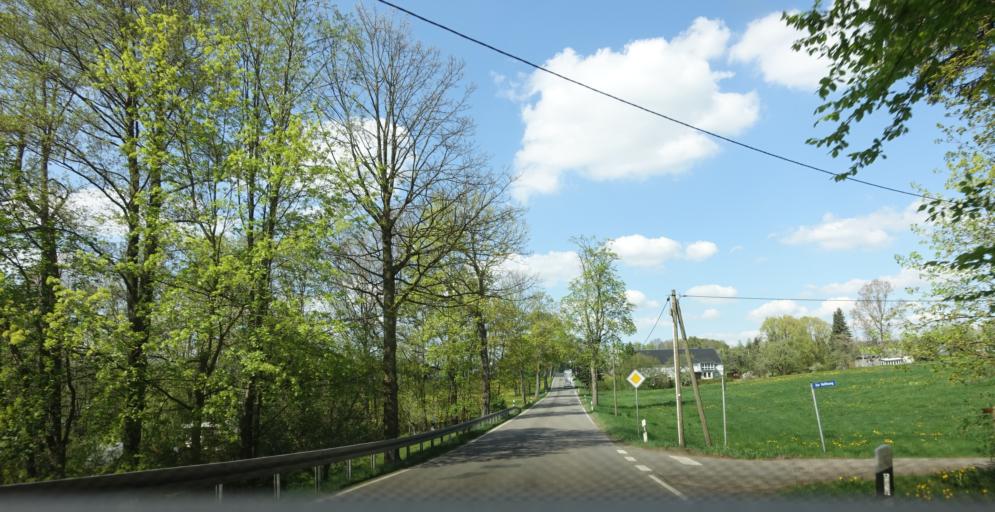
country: DE
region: Saxony
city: Brand-Erbisdorf
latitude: 50.8434
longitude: 13.3007
